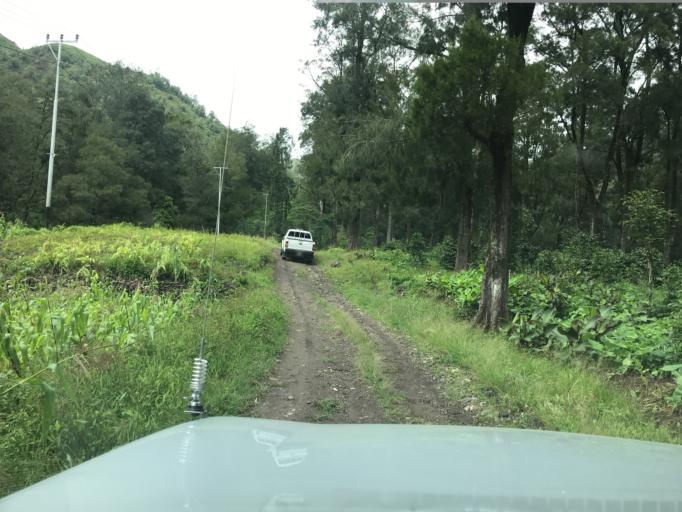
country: TL
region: Aileu
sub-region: Aileu Villa
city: Aileu
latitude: -8.8638
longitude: 125.5628
